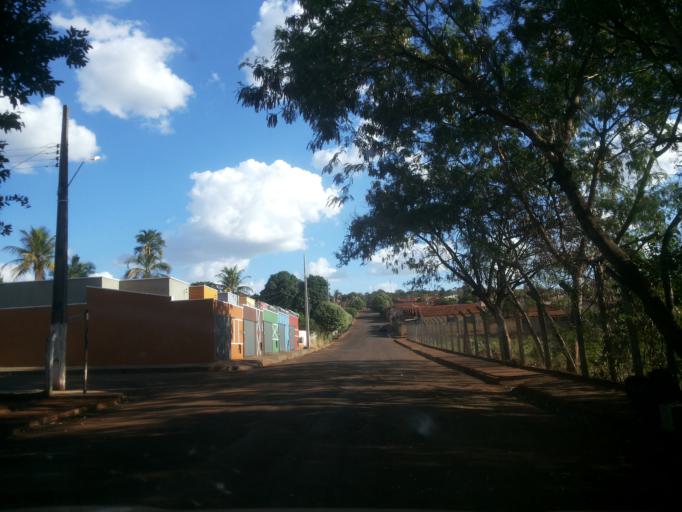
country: BR
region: Minas Gerais
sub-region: Capinopolis
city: Capinopolis
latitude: -18.6842
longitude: -49.5787
